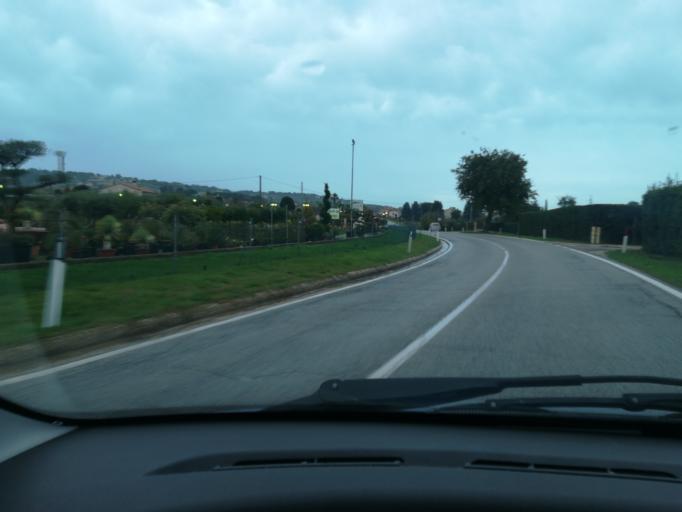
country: IT
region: The Marches
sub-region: Provincia di Macerata
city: Borgo Stazione
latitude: 43.2908
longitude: 13.6581
